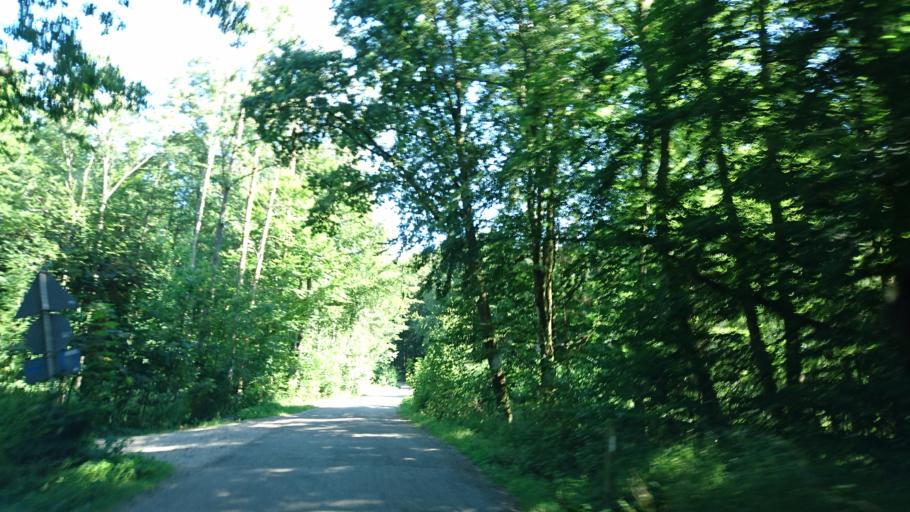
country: DE
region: Bavaria
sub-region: Swabia
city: Heretsried
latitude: 48.4760
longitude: 10.7546
